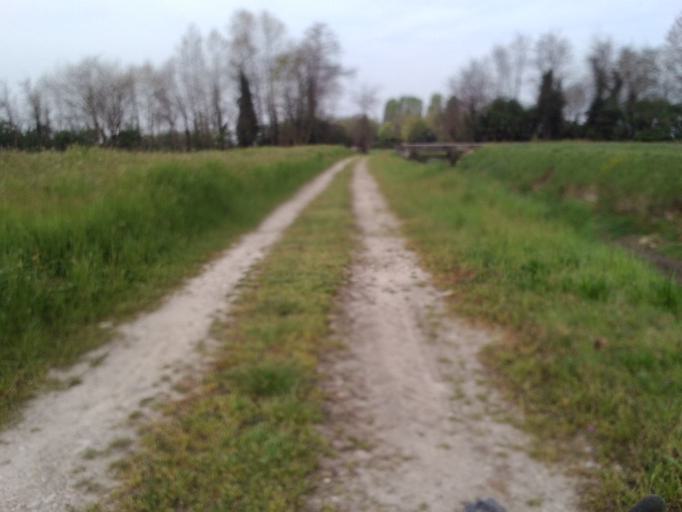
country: IT
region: Veneto
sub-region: Provincia di Verona
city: Villafranca di Verona
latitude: 45.3357
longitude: 10.8581
